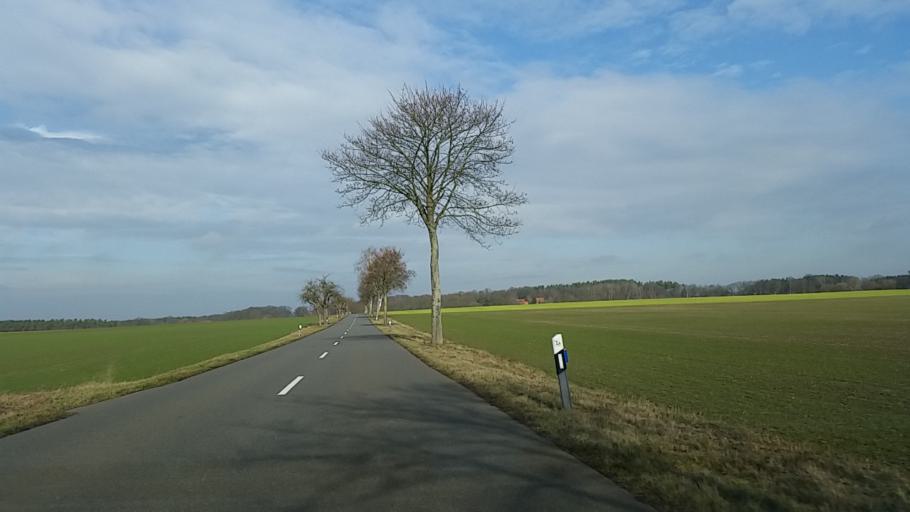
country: DE
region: Lower Saxony
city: Altenmedingen
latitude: 53.1605
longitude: 10.6194
